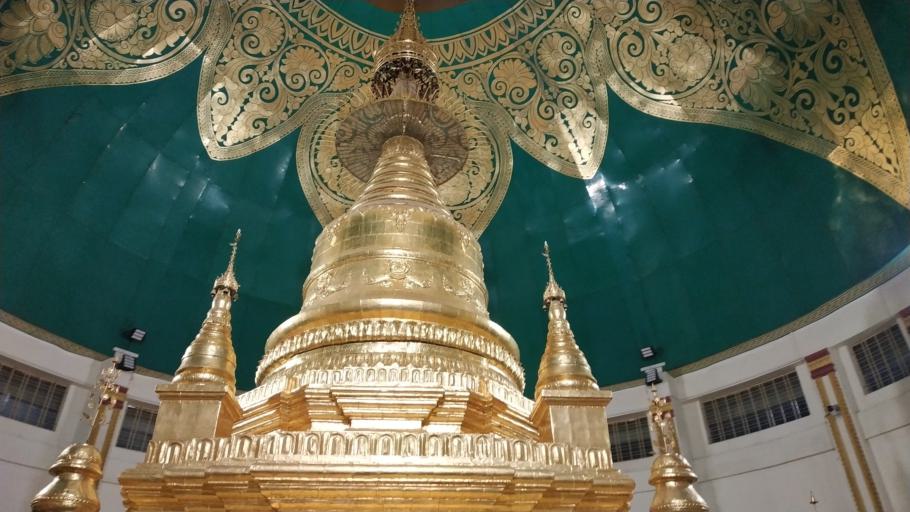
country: MM
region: Mandalay
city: Mandalay
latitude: 21.9773
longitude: 96.1107
